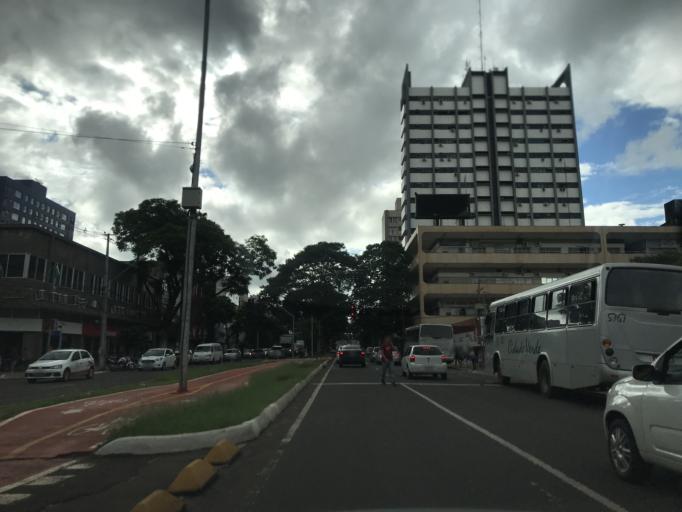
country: BR
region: Parana
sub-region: Maringa
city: Maringa
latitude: -23.4209
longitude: -51.9379
